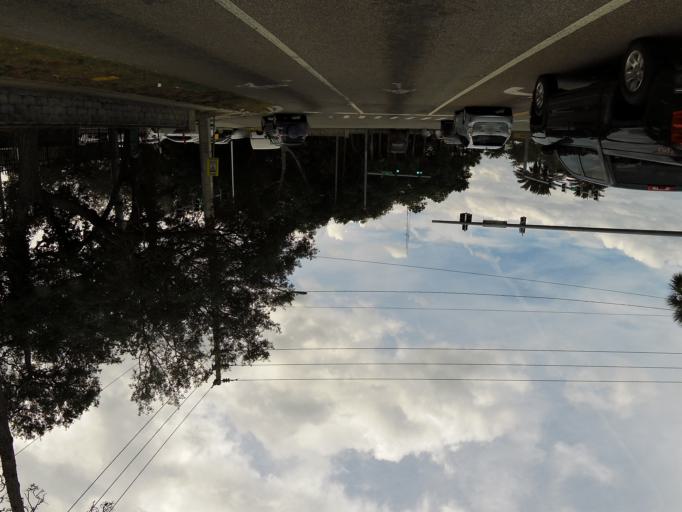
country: US
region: Florida
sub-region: Duval County
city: Jacksonville Beach
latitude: 30.2886
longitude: -81.4057
